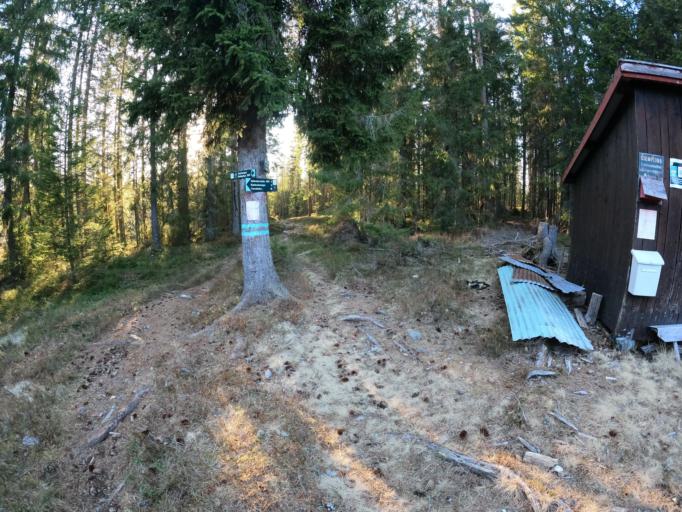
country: NO
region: Akershus
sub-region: Nittedal
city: Aneby
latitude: 60.1135
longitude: 10.9361
